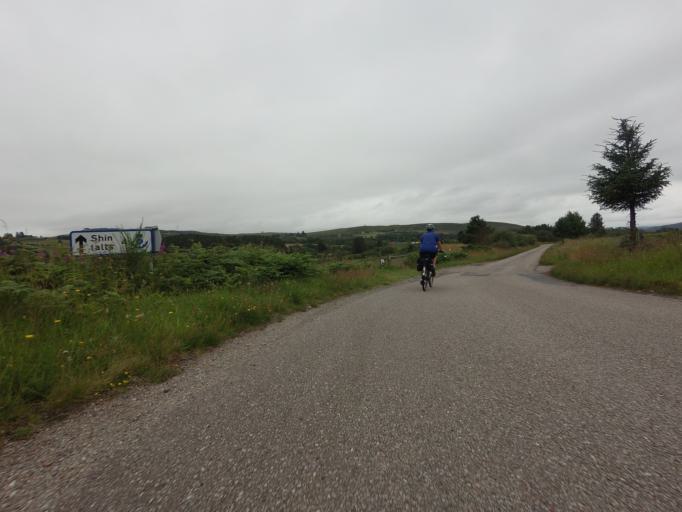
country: GB
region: Scotland
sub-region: Highland
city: Alness
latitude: 58.0115
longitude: -4.4030
